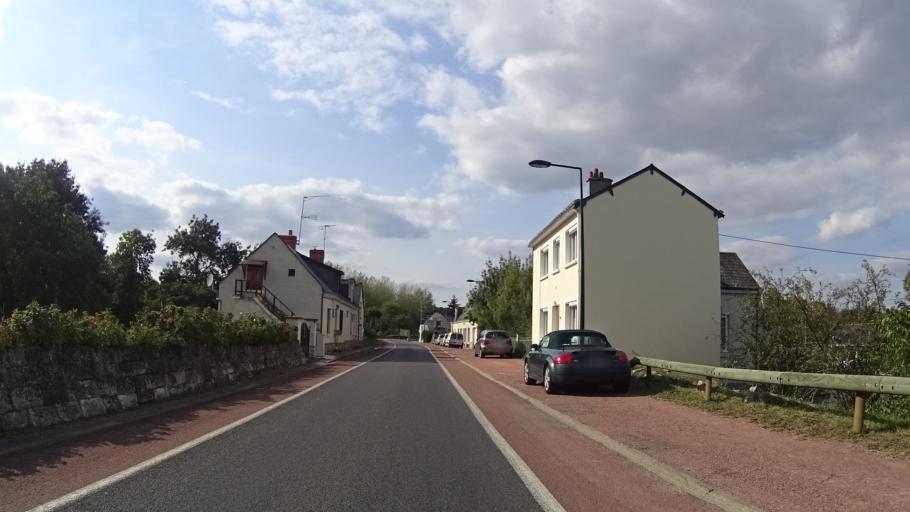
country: FR
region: Pays de la Loire
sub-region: Departement de Maine-et-Loire
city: Saint-Martin-de-la-Place
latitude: 47.3127
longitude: -0.1434
